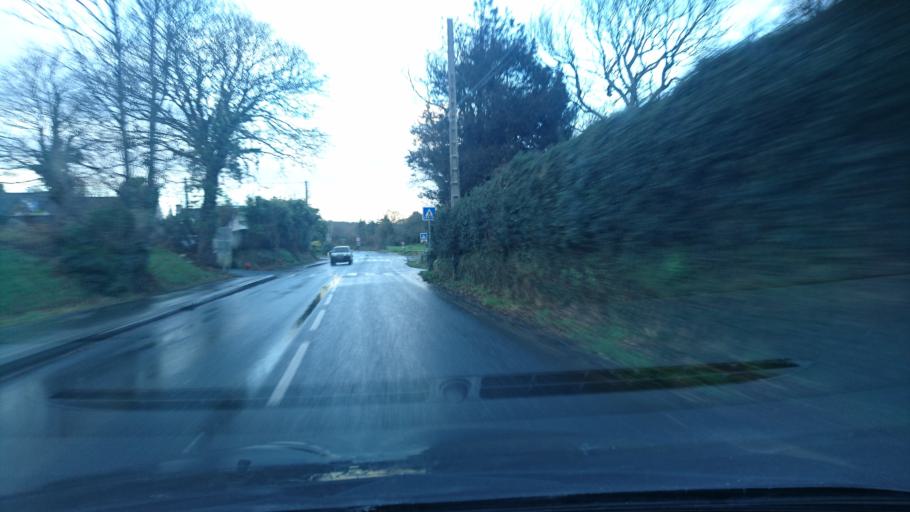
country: FR
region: Brittany
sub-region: Departement du Finistere
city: Guilers
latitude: 48.3991
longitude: -4.5398
